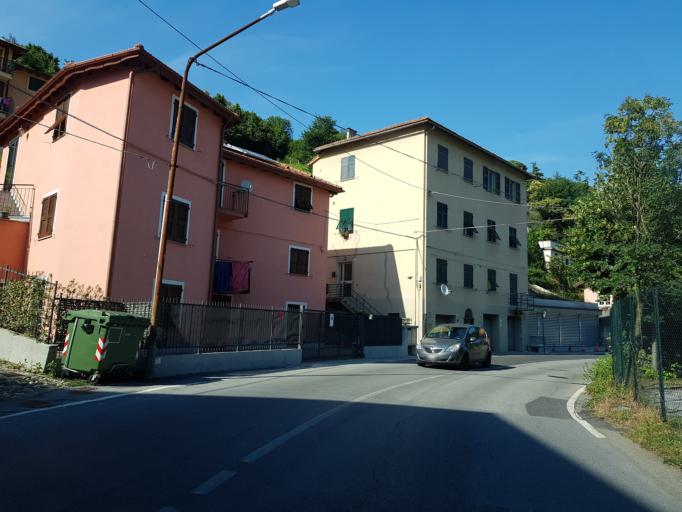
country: IT
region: Liguria
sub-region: Provincia di Genova
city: Manesseno
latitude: 44.4780
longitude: 8.9316
